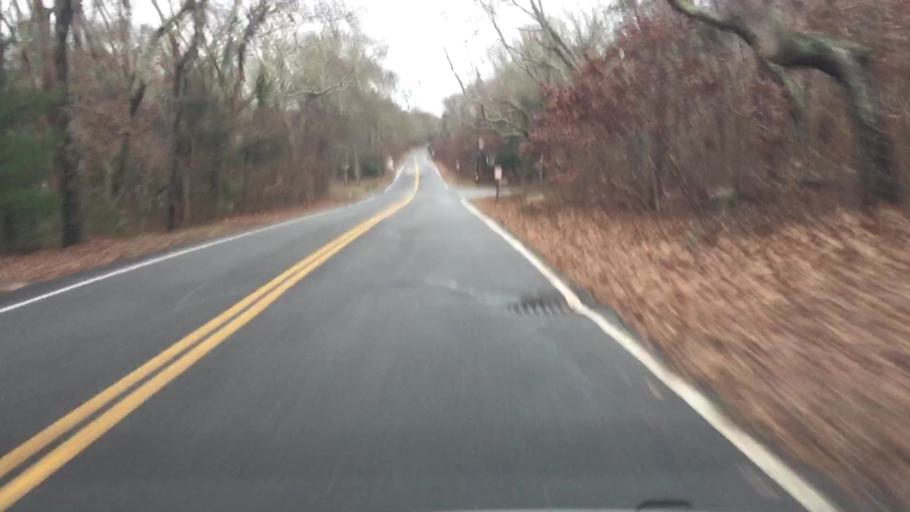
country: US
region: Massachusetts
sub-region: Barnstable County
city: West Falmouth
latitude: 41.6181
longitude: -70.6391
